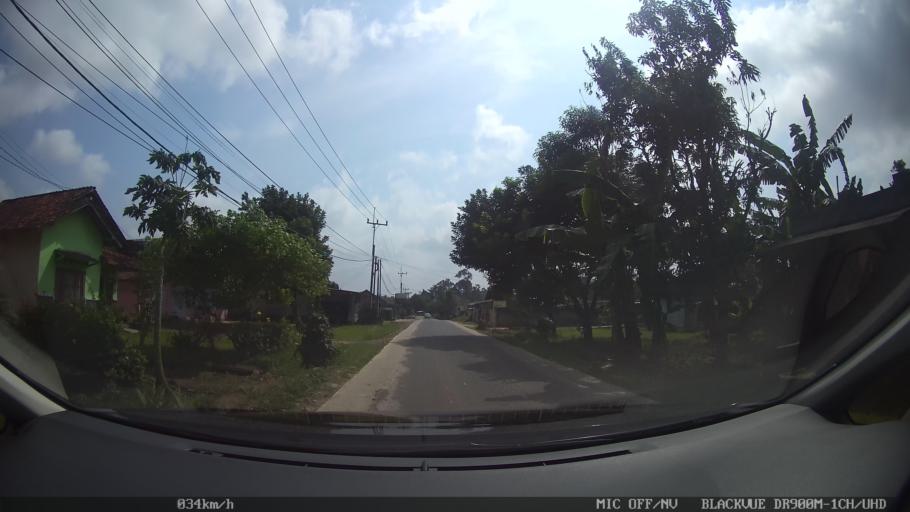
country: ID
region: Lampung
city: Kedaton
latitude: -5.3323
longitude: 105.2809
